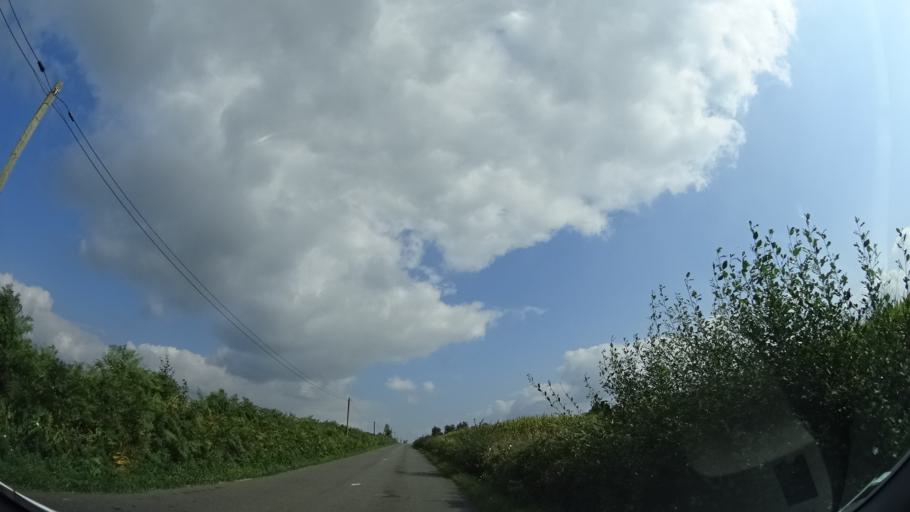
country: FR
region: Brittany
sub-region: Departement d'Ille-et-Vilaine
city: Pleumeleuc
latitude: 48.1924
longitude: -1.9100
